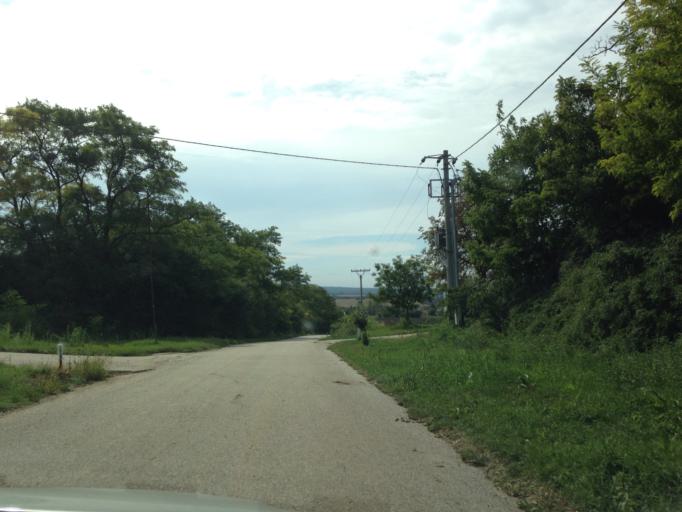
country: SK
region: Nitriansky
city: Svodin
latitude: 47.9123
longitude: 18.4269
